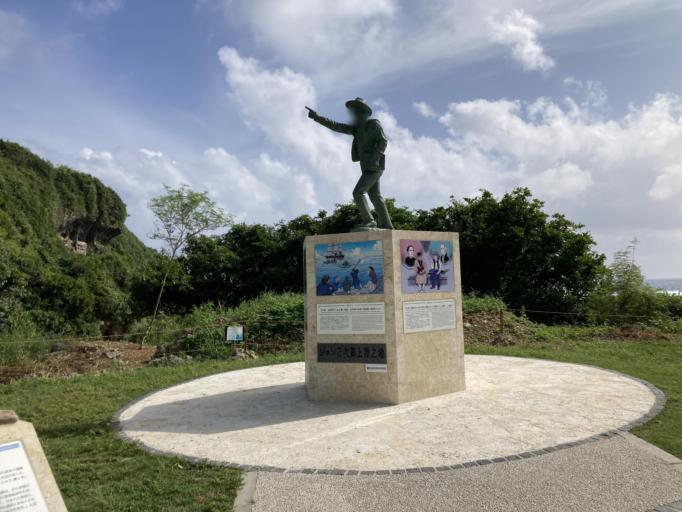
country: JP
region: Okinawa
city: Itoman
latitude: 26.0899
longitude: 127.7103
